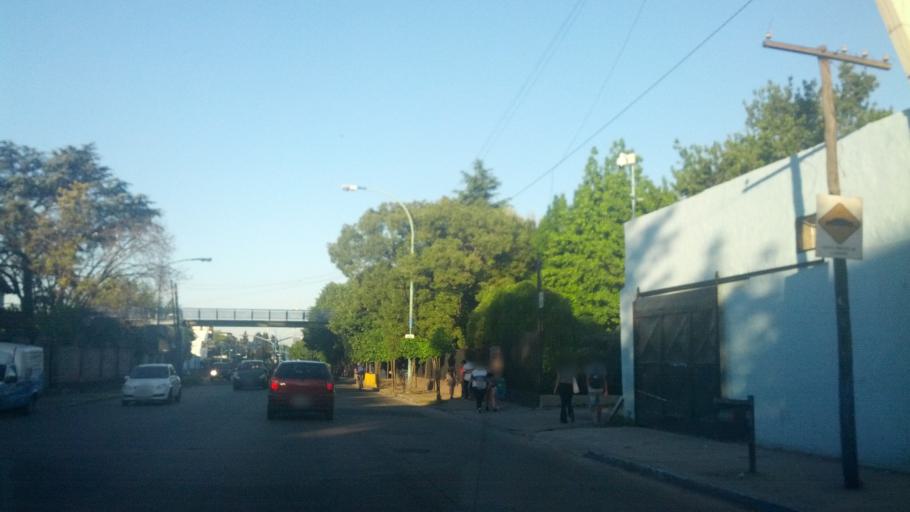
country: AR
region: Buenos Aires
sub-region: Partido de Lomas de Zamora
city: Lomas de Zamora
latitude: -34.7817
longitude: -58.3998
